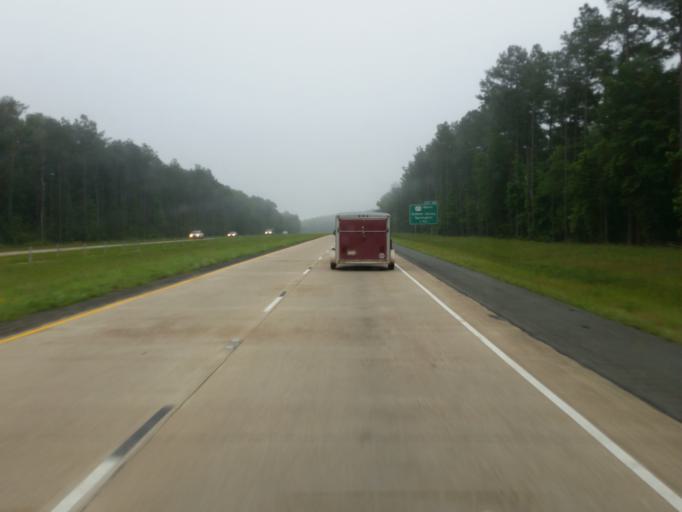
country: US
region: Louisiana
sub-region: Webster Parish
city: Minden
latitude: 32.5859
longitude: -93.3575
